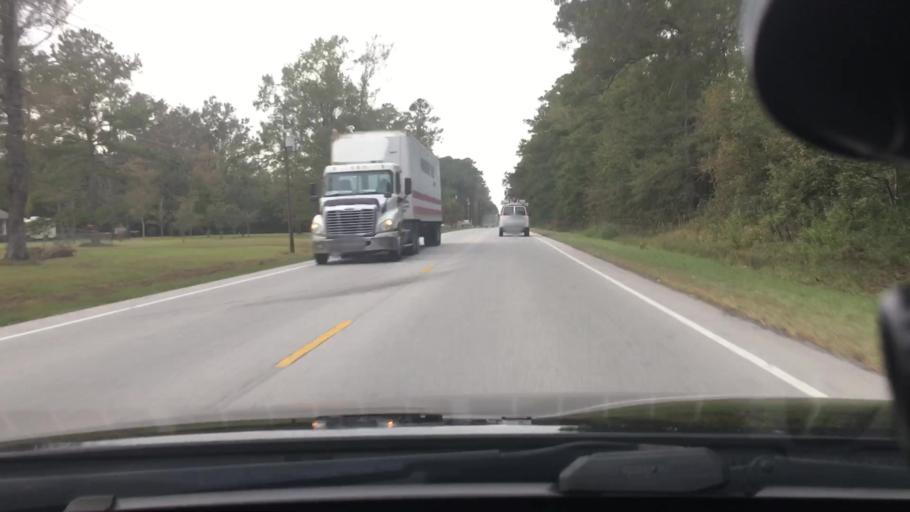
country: US
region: North Carolina
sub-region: Craven County
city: New Bern
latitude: 35.2035
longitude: -77.0581
